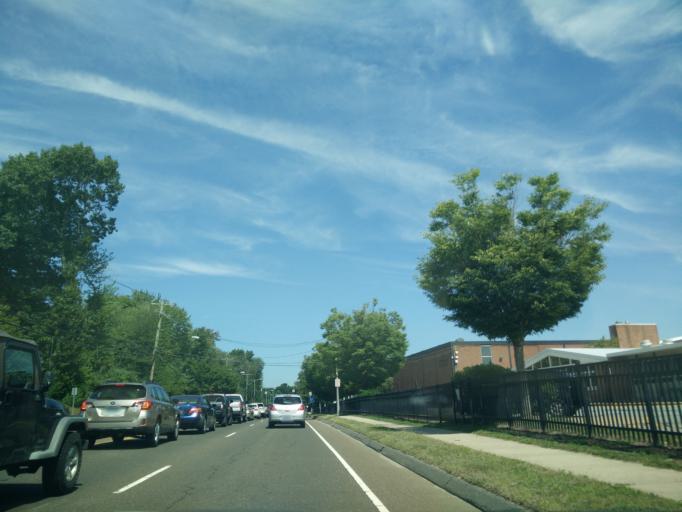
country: US
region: Connecticut
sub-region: Middlesex County
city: Clinton
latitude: 41.2904
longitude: -72.5297
